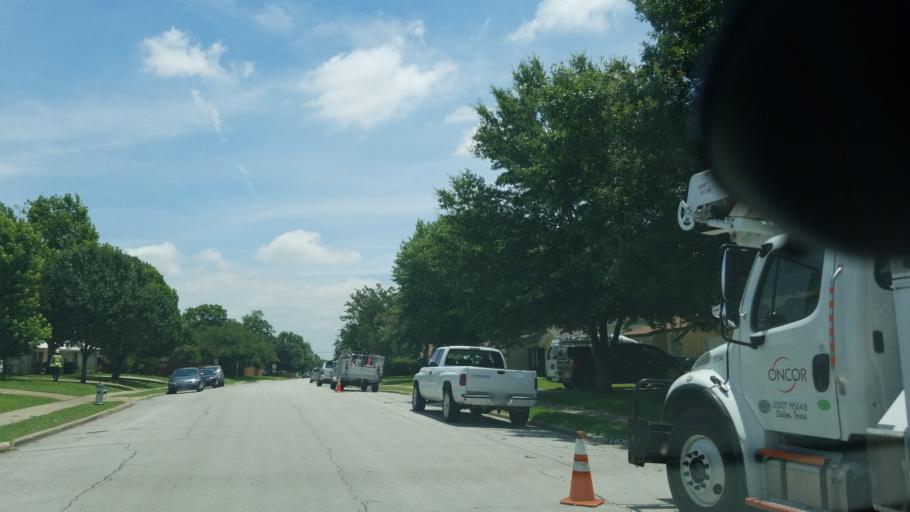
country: US
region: Texas
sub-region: Dallas County
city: Irving
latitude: 32.8510
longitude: -96.9742
